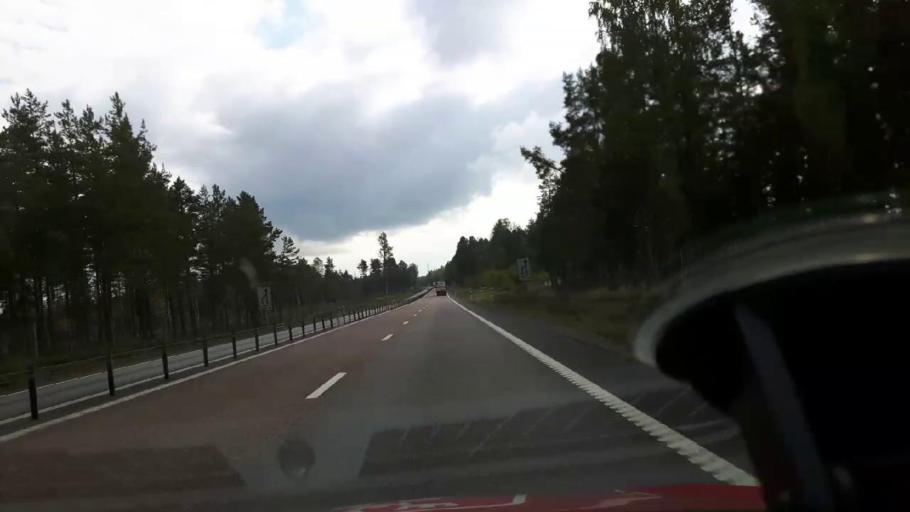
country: SE
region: Gaevleborg
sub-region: Gavle Kommun
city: Norrsundet
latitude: 60.9773
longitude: 17.0197
